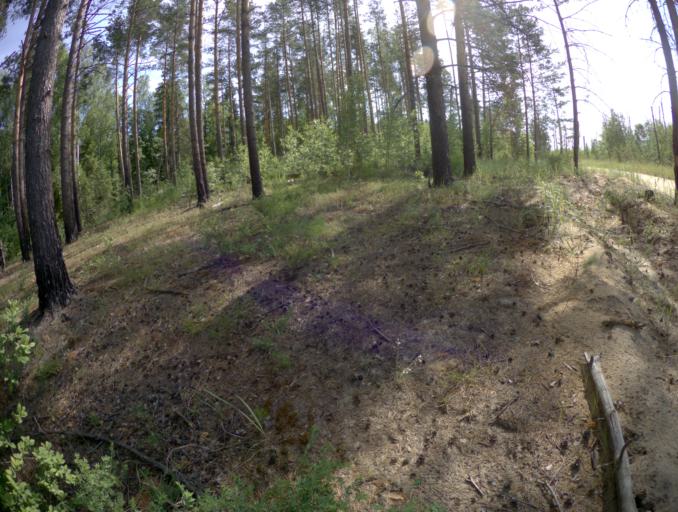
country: RU
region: Ivanovo
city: Talitsy
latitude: 56.5123
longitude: 42.3756
